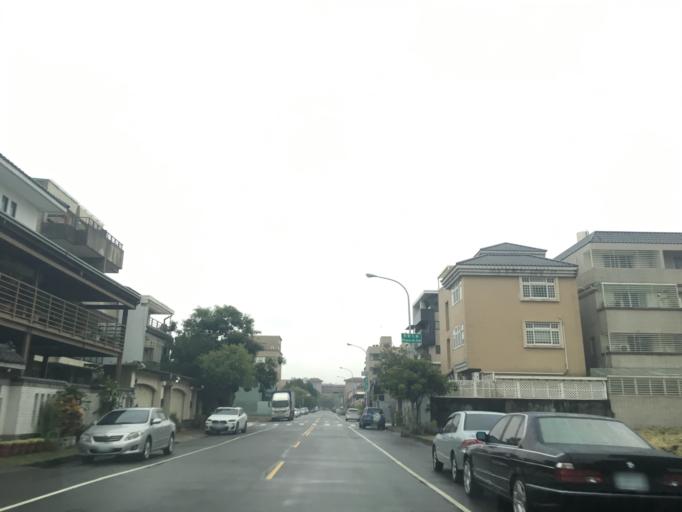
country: TW
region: Taiwan
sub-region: Taichung City
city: Taichung
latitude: 24.1660
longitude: 120.7079
